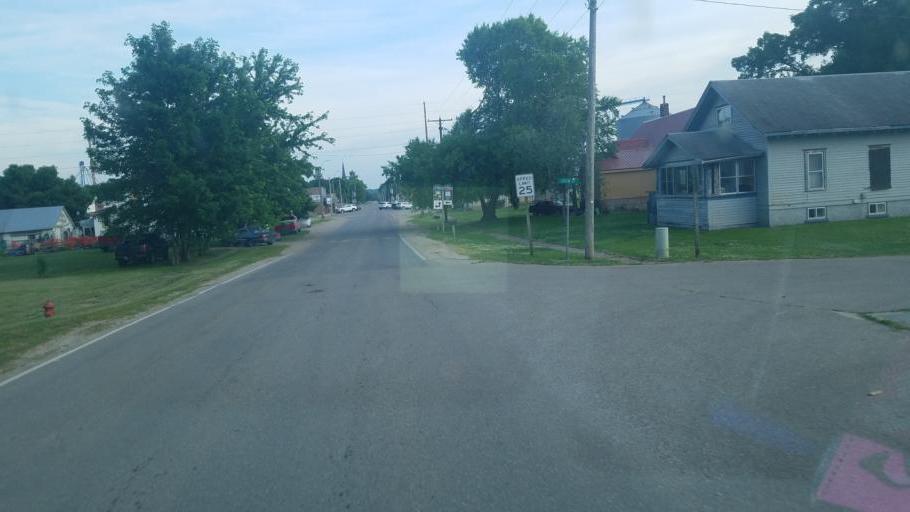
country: US
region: Iowa
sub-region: Benton County
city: Belle Plaine
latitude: 41.9215
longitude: -92.3947
